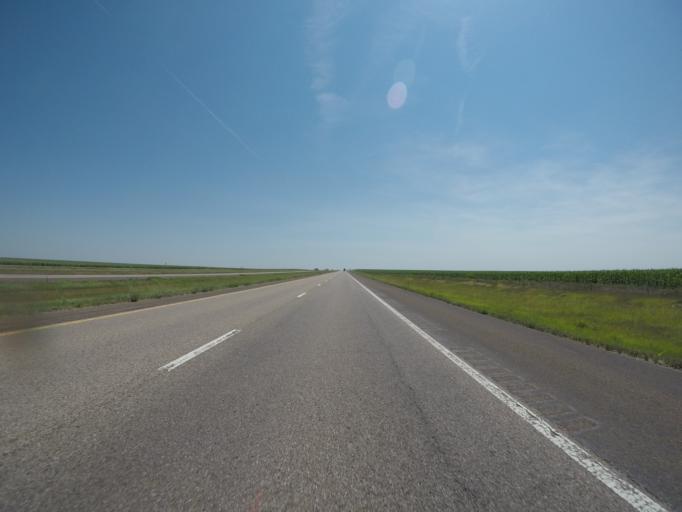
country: US
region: Kansas
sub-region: Thomas County
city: Colby
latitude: 39.3660
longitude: -101.2352
